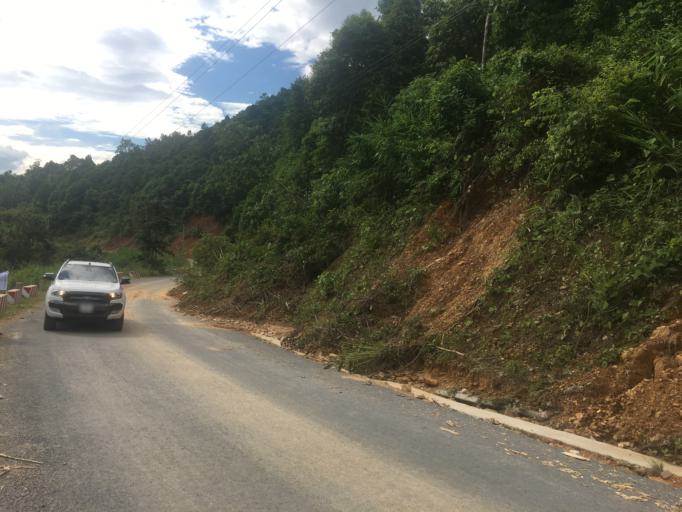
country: VN
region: Ha Giang
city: Thanh Pho Ha Giang
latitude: 22.8554
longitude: 105.0441
